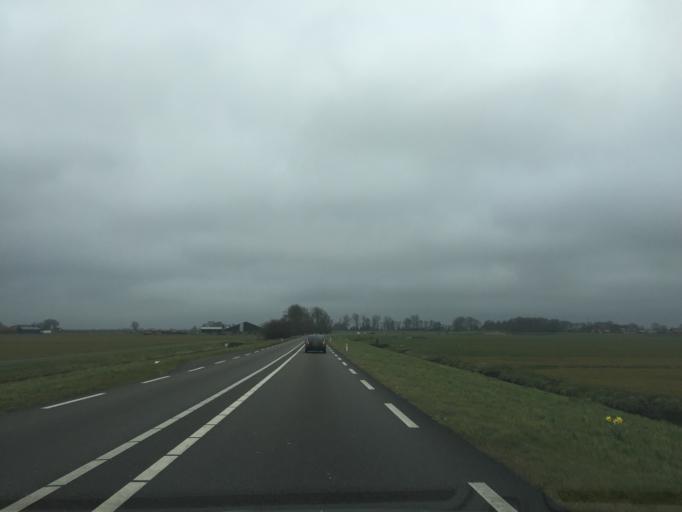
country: NL
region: South Holland
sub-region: Gemeente Kaag en Braassem
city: Leimuiden
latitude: 52.1985
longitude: 4.6798
